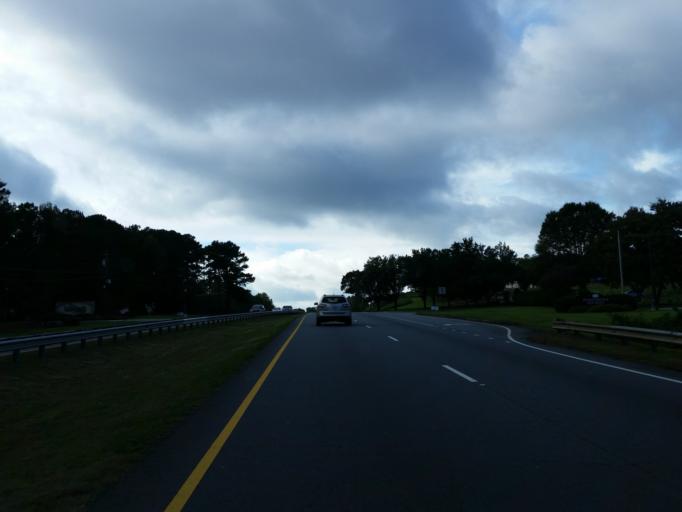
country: US
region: Georgia
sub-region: Cobb County
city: Kennesaw
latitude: 34.0237
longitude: -84.6292
